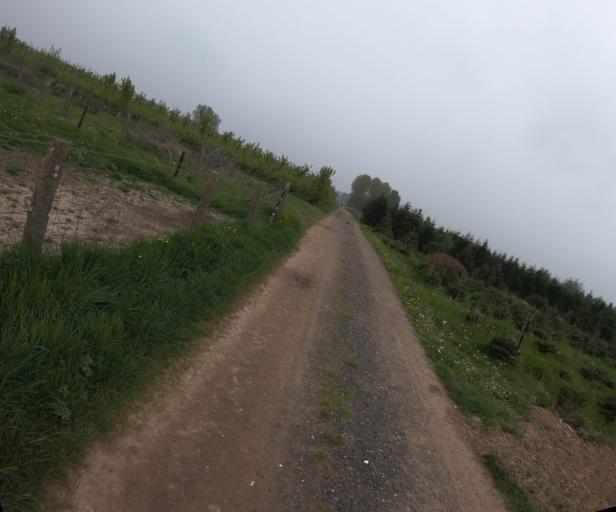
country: BE
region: Flanders
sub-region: Provincie Vlaams-Brabant
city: Gooik
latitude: 50.7840
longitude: 4.1252
